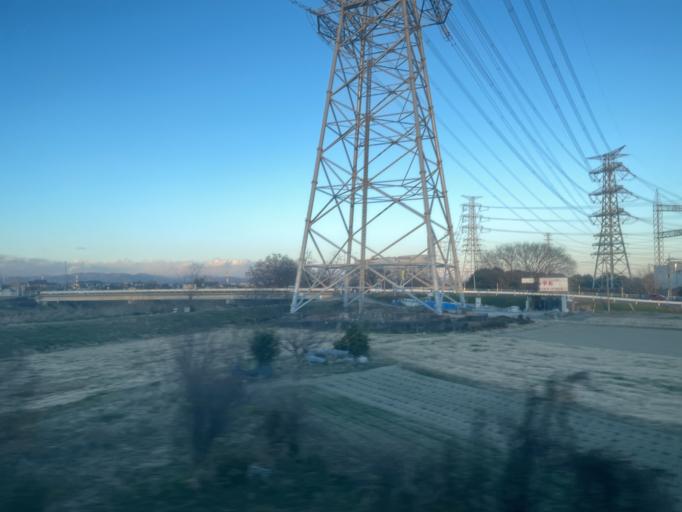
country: JP
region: Saitama
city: Honjo
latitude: 36.2211
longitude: 139.2086
